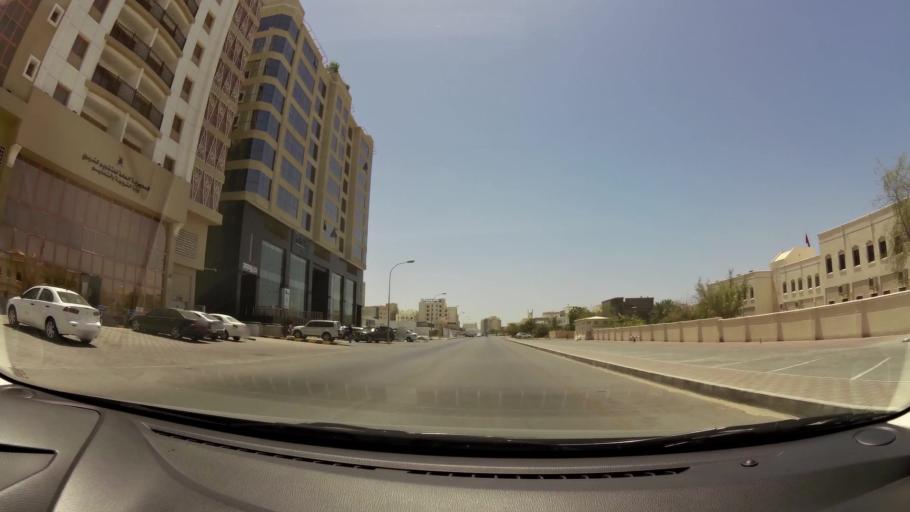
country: OM
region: Muhafazat Masqat
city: Bawshar
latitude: 23.5908
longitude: 58.3813
